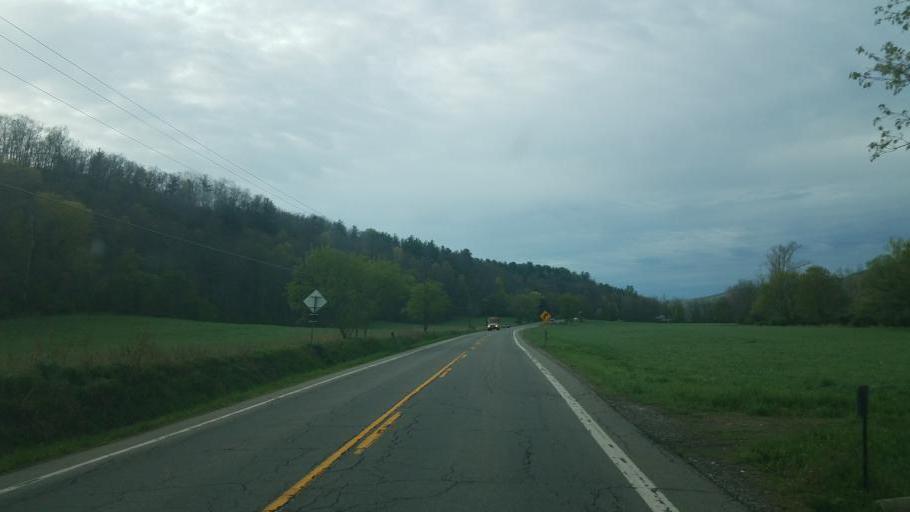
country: US
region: New York
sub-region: Steuben County
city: Canisteo
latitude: 42.2421
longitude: -77.5823
